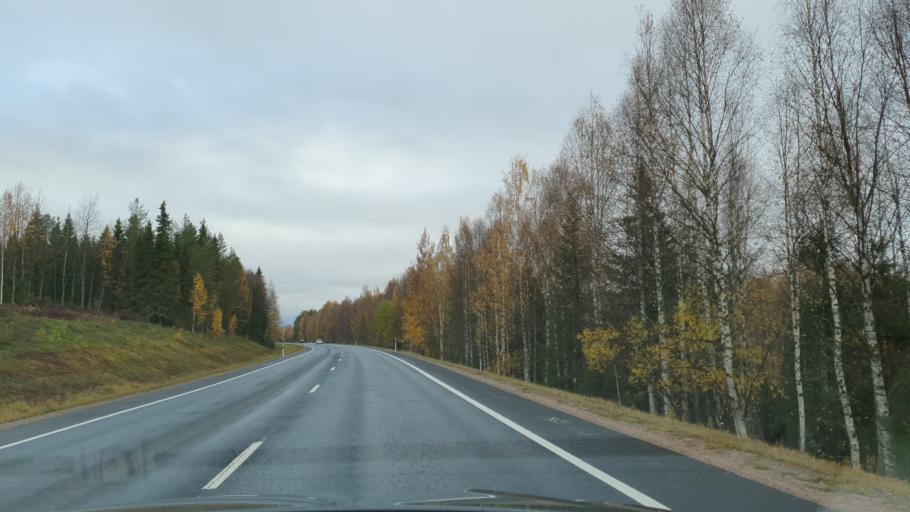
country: FI
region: Lapland
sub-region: Rovaniemi
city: Rovaniemi
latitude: 66.6284
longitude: 25.5267
